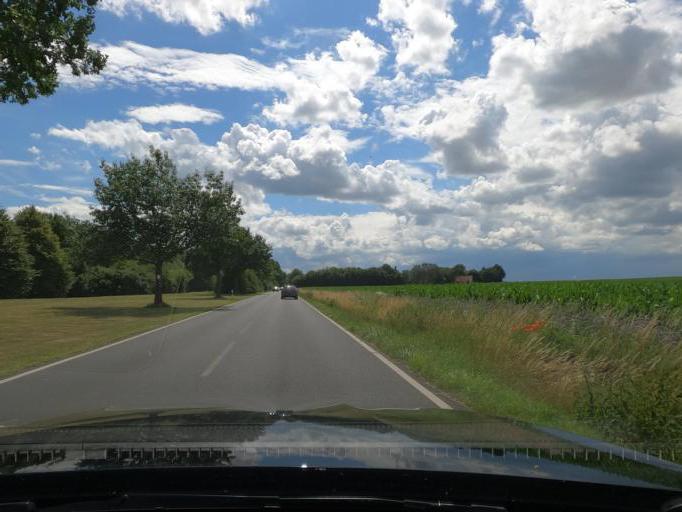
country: DE
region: Lower Saxony
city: Lengede
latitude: 52.1656
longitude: 10.3026
